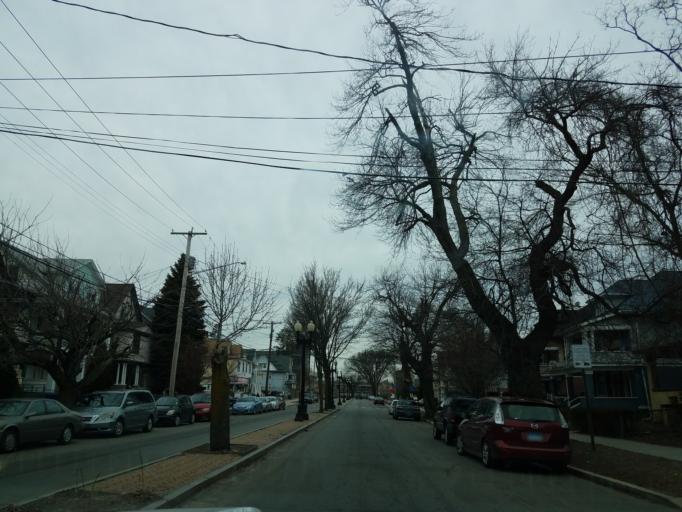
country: US
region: Connecticut
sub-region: Fairfield County
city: Bridgeport
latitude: 41.1669
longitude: -73.1925
